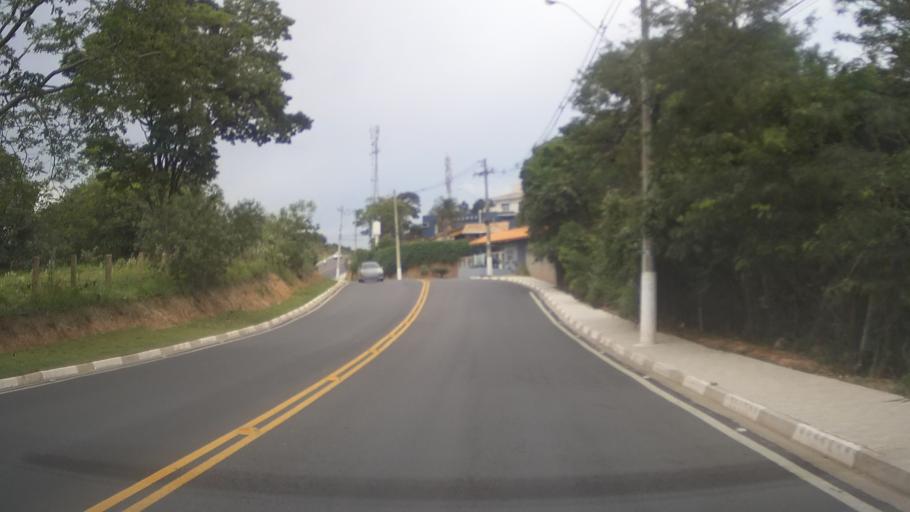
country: BR
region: Sao Paulo
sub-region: Itupeva
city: Itupeva
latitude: -23.1633
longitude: -47.0728
